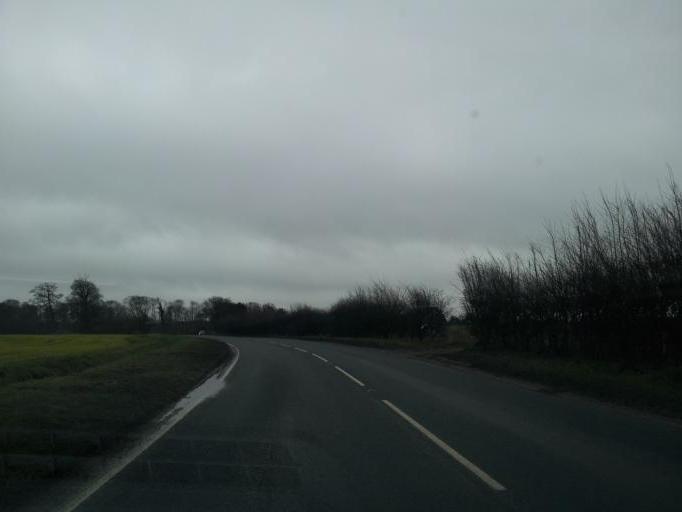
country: GB
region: England
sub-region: Essex
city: Manningtree
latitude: 51.9342
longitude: 1.0703
